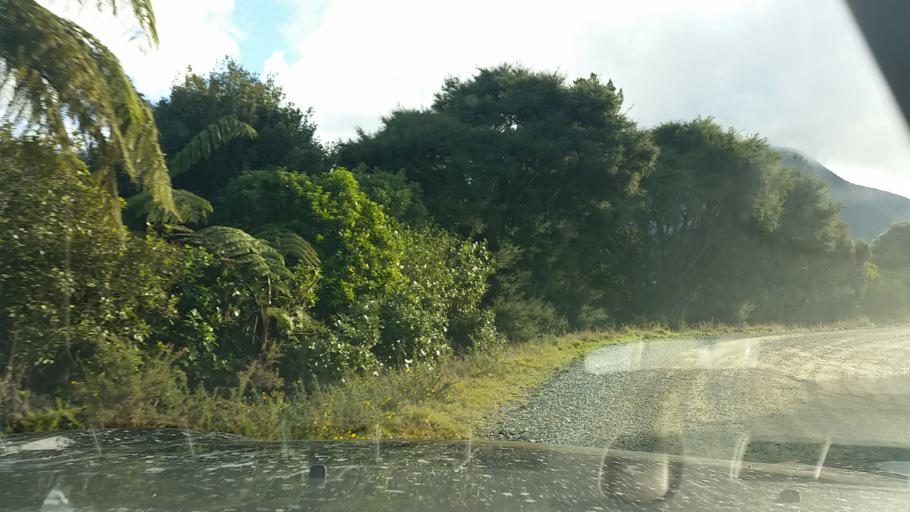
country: NZ
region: Marlborough
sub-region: Marlborough District
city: Picton
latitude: -41.1290
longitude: 174.1416
